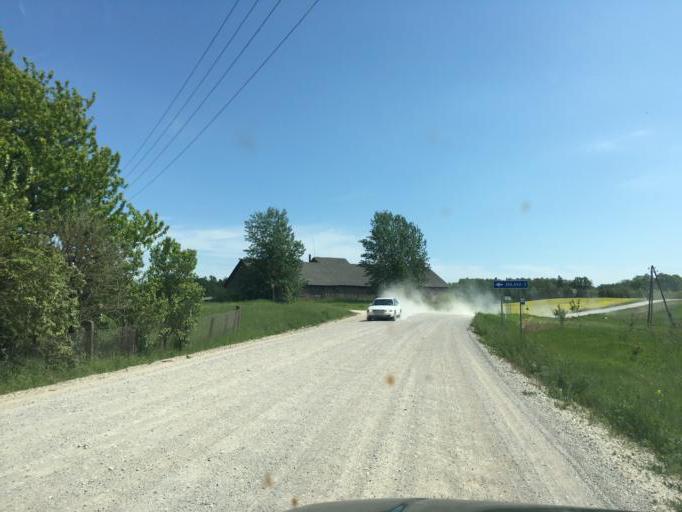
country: LV
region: Talsu Rajons
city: Valdemarpils
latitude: 57.3770
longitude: 22.6206
